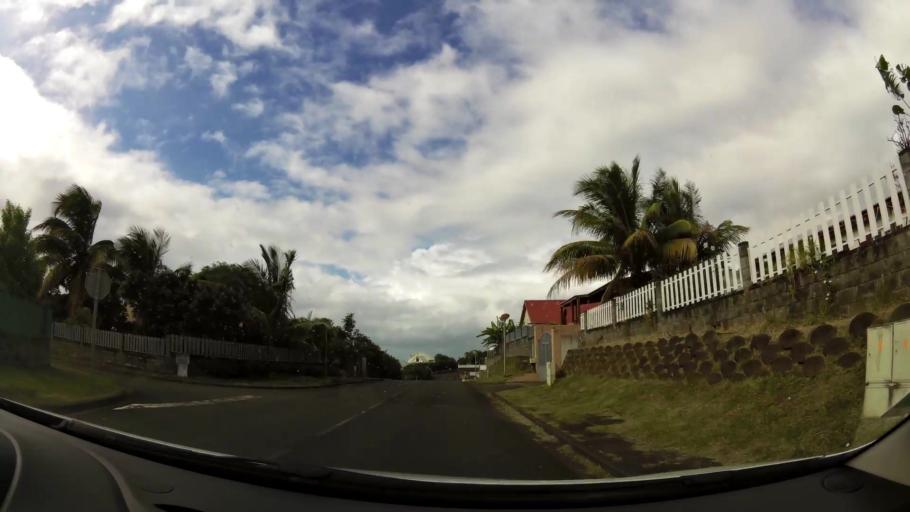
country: RE
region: Reunion
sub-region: Reunion
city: Sainte-Marie
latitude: -20.8957
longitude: 55.5704
